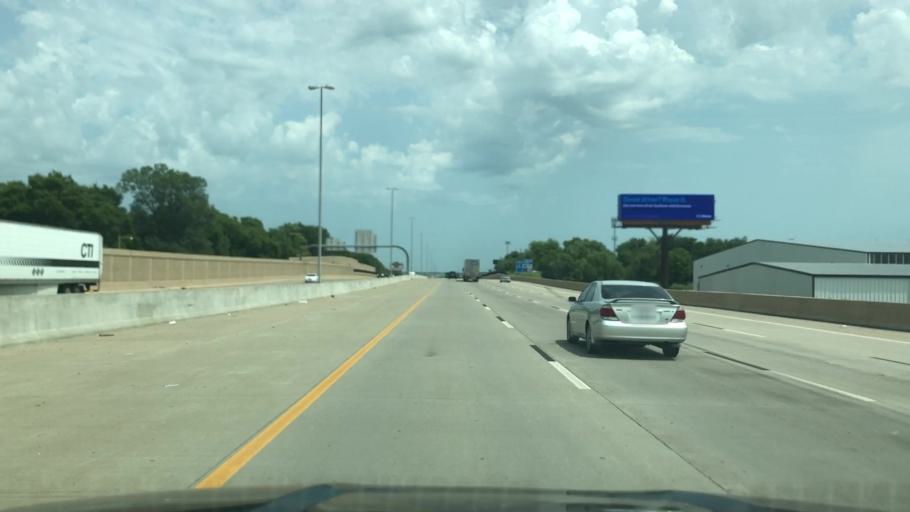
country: US
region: Oklahoma
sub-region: Rogers County
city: Catoosa
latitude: 36.1624
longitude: -95.7788
